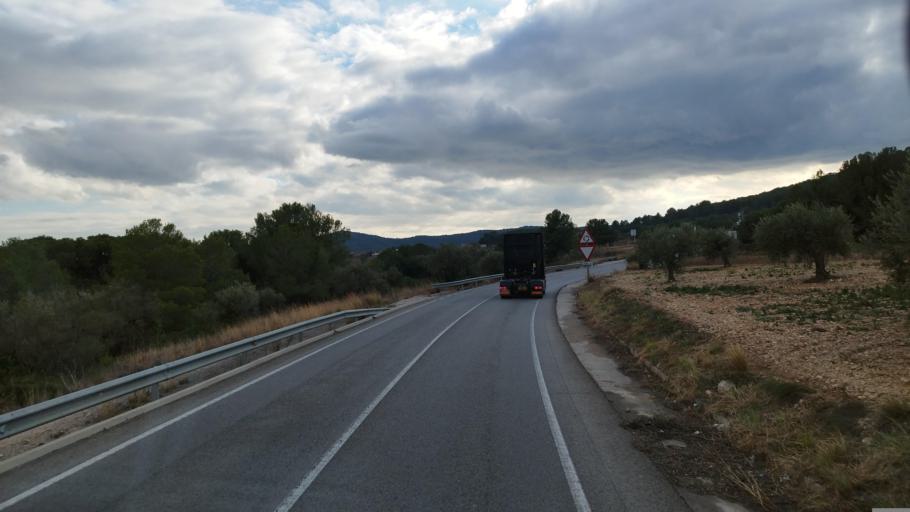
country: ES
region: Catalonia
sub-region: Provincia de Tarragona
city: Albinyana
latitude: 41.2624
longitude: 1.4977
